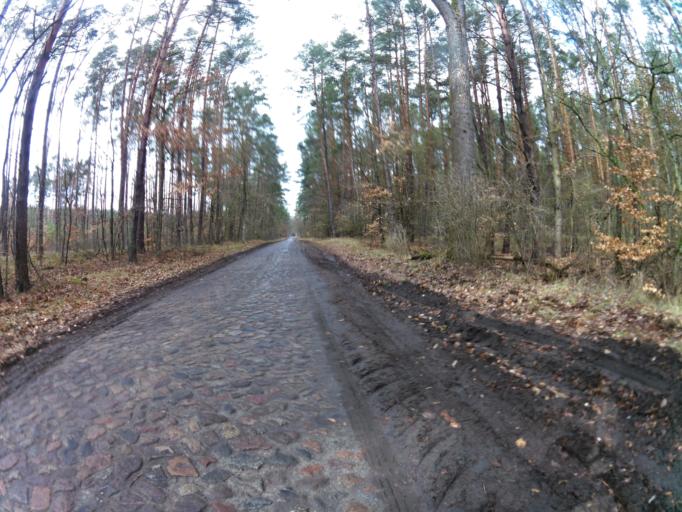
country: PL
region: West Pomeranian Voivodeship
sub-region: Powiat mysliborski
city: Debno
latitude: 52.7266
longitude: 14.7287
